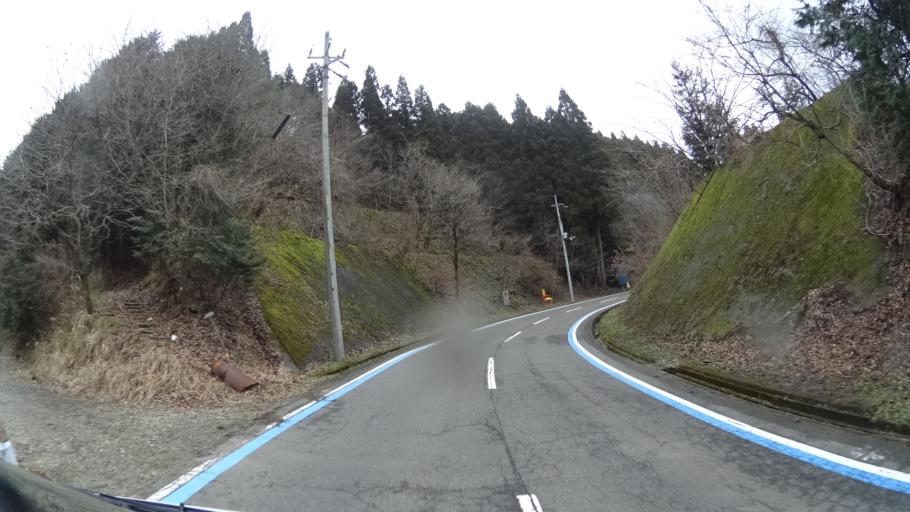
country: JP
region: Kyoto
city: Maizuru
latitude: 35.4129
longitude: 135.4101
